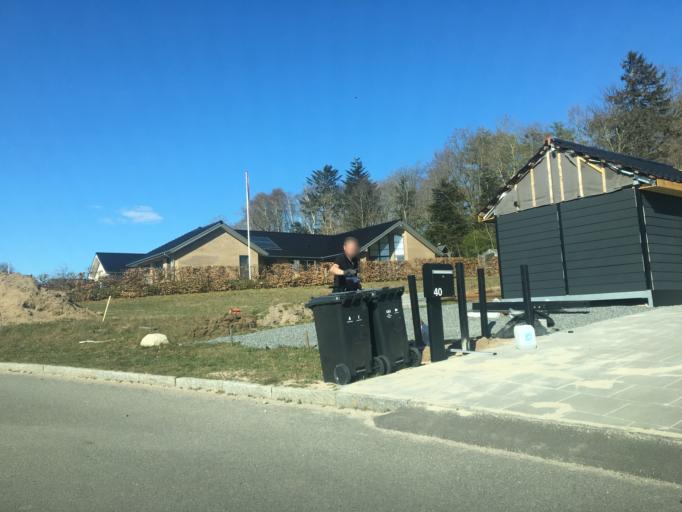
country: DK
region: Zealand
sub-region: Naestved Kommune
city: Fensmark
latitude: 55.2569
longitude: 11.8555
